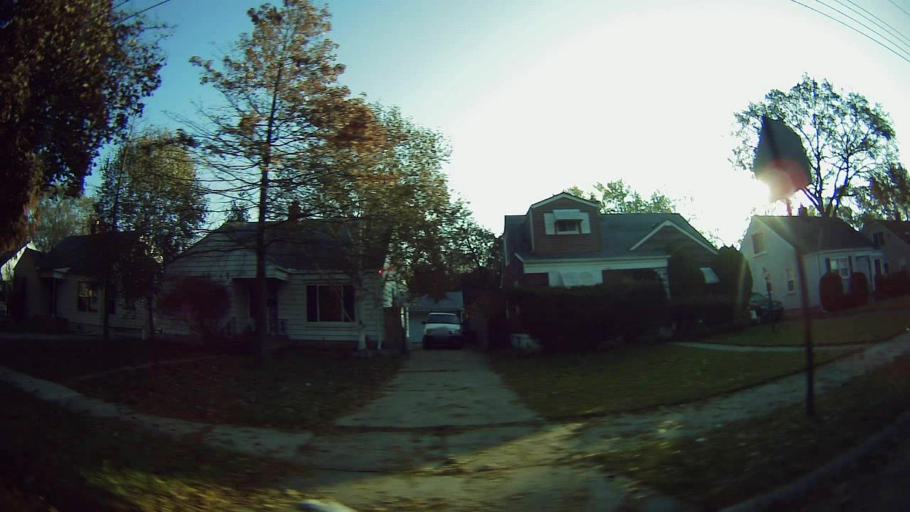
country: US
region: Michigan
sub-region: Oakland County
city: Huntington Woods
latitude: 42.4634
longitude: -83.1623
